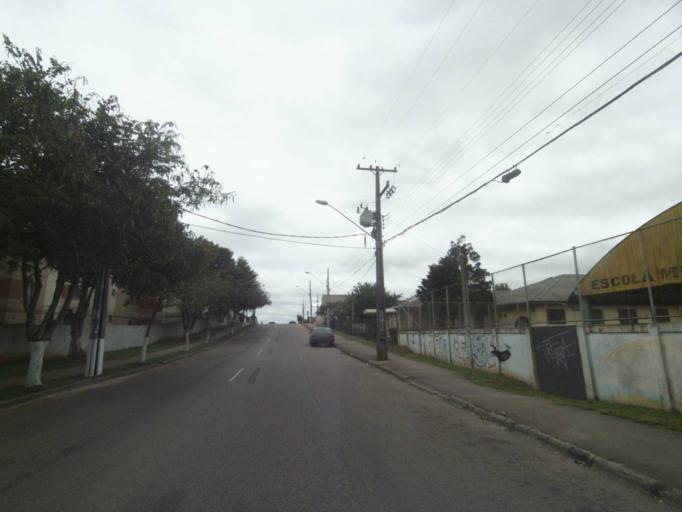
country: BR
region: Parana
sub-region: Sao Jose Dos Pinhais
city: Sao Jose dos Pinhais
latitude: -25.5473
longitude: -49.2678
